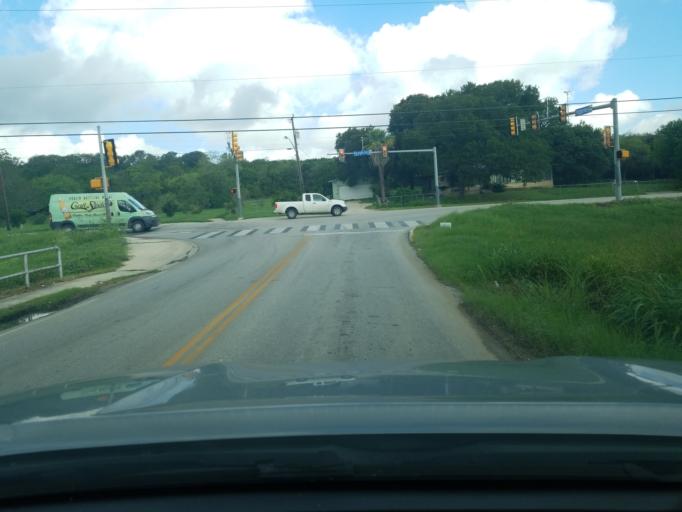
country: US
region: Texas
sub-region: Bexar County
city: Live Oak
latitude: 29.5830
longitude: -98.3652
